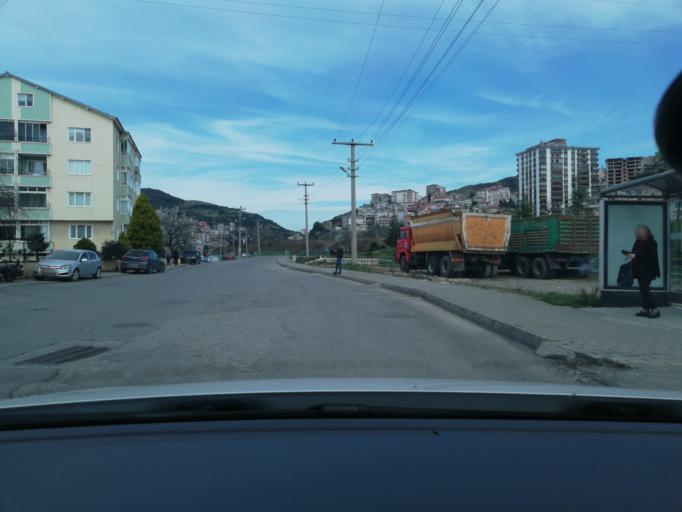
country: TR
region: Zonguldak
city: Eregli
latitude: 41.2923
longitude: 31.4077
